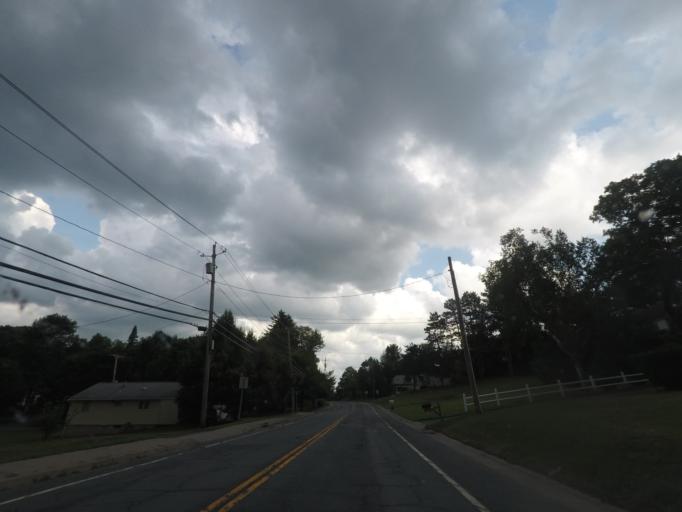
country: US
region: New York
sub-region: Rensselaer County
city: Wynantskill
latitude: 42.6905
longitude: -73.6416
